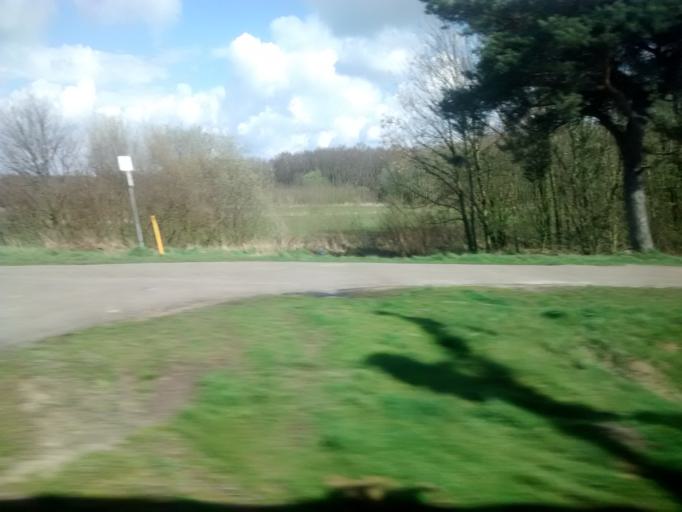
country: NL
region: Limburg
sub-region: Gemeente Weert
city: Weert
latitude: 51.2677
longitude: 5.6585
